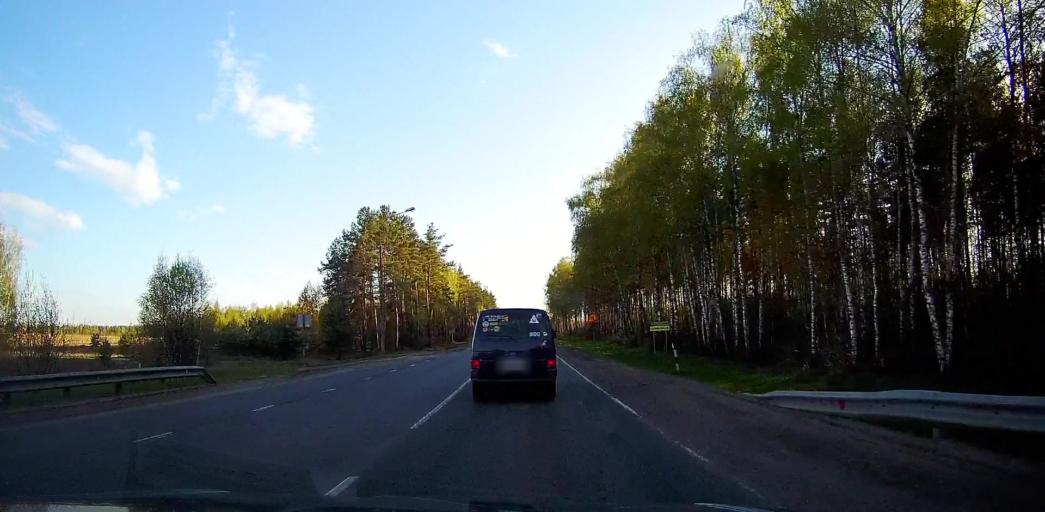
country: RU
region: Moskovskaya
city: Gzhel'
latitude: 55.6400
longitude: 38.3672
